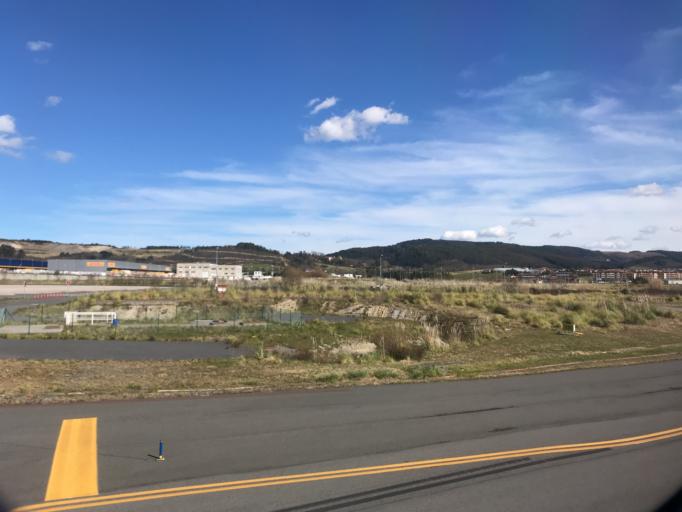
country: ES
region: Basque Country
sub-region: Bizkaia
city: Sondika
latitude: 43.3005
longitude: -2.9038
